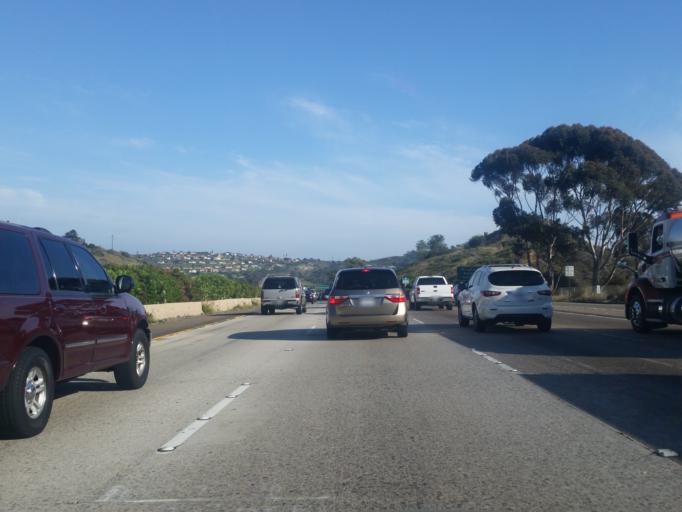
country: US
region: California
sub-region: San Diego County
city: Solana Beach
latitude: 33.0157
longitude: -117.2708
